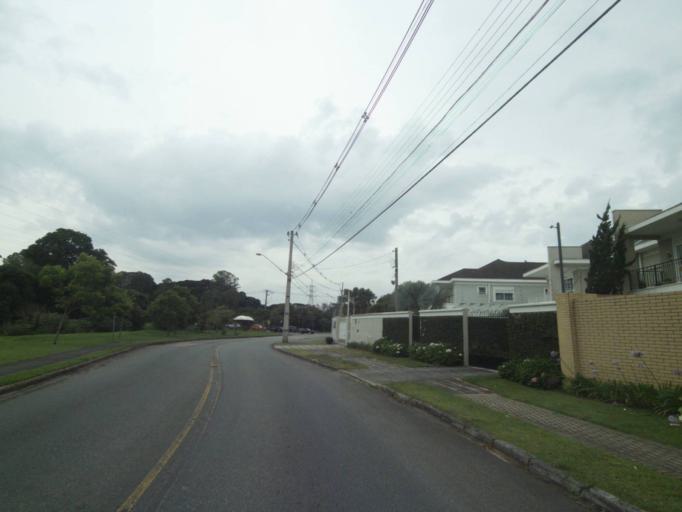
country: BR
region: Parana
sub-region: Curitiba
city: Curitiba
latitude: -25.4054
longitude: -49.3028
